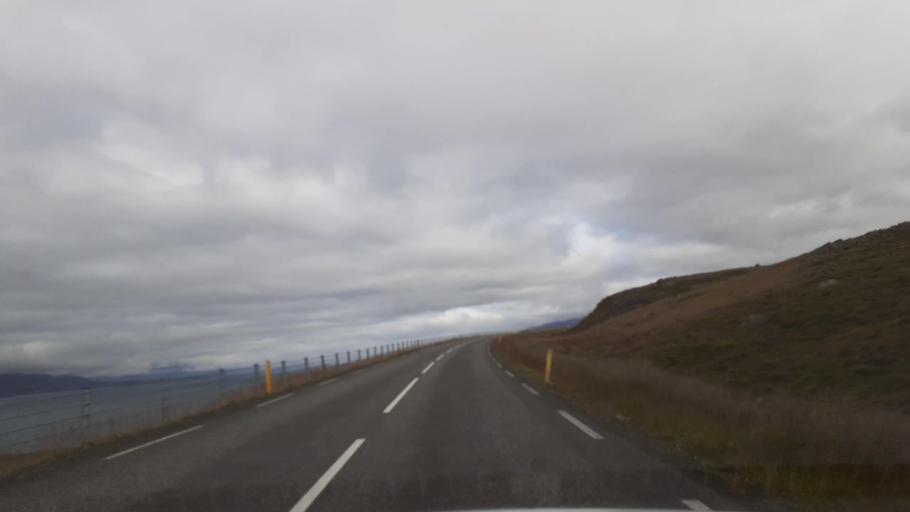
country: IS
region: Northeast
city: Akureyri
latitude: 65.8250
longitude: -18.0559
